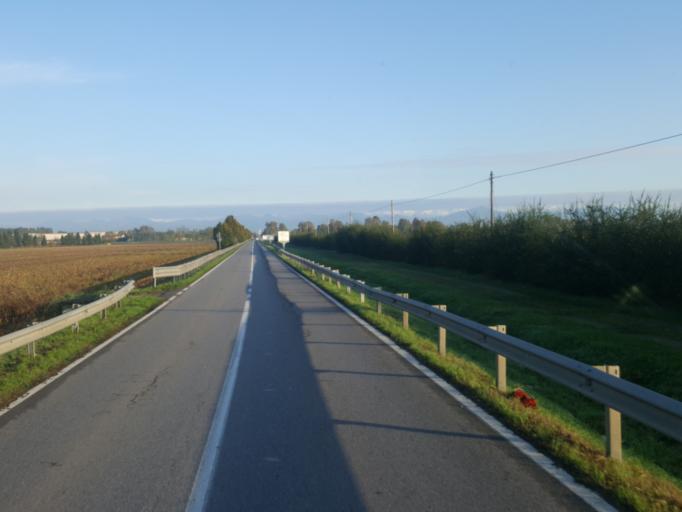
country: IT
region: Lombardy
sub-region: Provincia di Bergamo
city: Morengo
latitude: 45.5466
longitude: 9.7063
